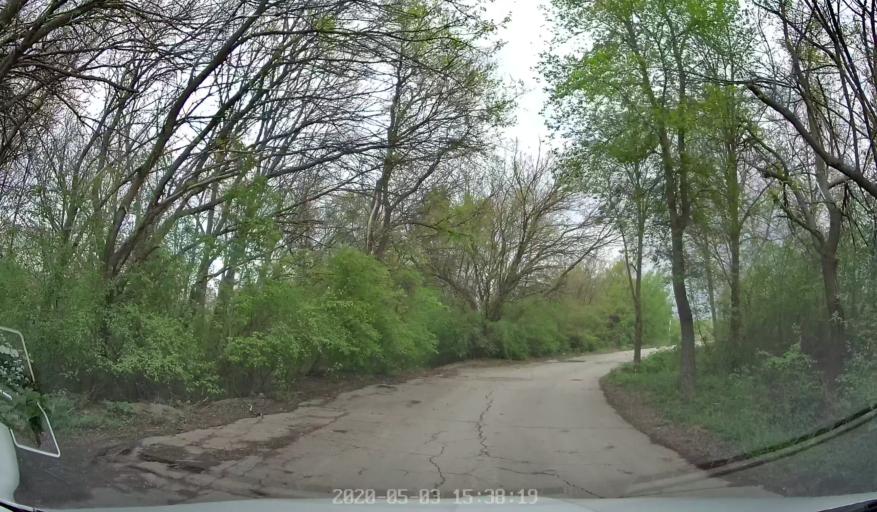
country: MD
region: Chisinau
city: Vatra
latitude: 47.0978
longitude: 28.7075
